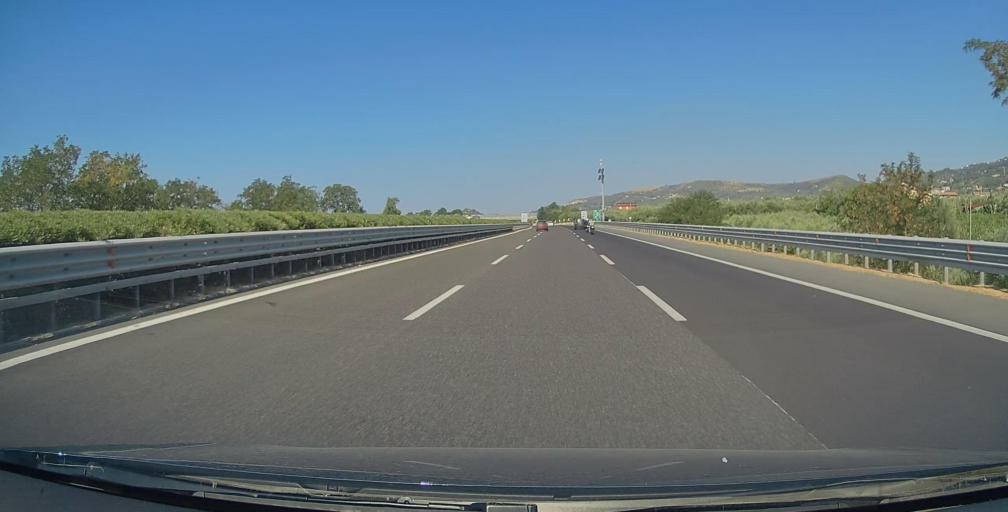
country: IT
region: Campania
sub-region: Provincia di Salerno
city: Quadrivio
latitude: 40.6098
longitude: 15.0858
